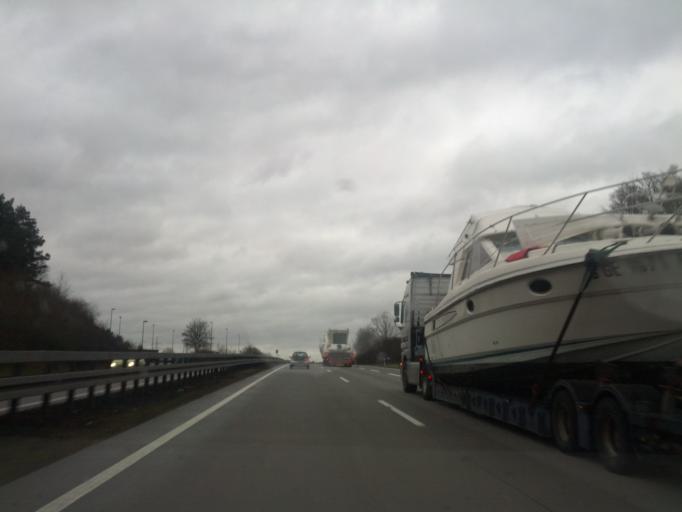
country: DE
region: Hesse
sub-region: Regierungsbezirk Giessen
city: Lich
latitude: 50.5179
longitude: 8.7541
